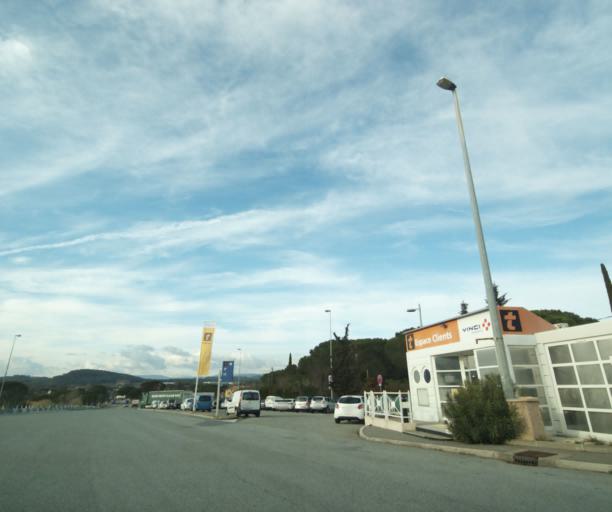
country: FR
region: Provence-Alpes-Cote d'Azur
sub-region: Departement du Var
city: Le Muy
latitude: 43.4612
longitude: 6.5506
